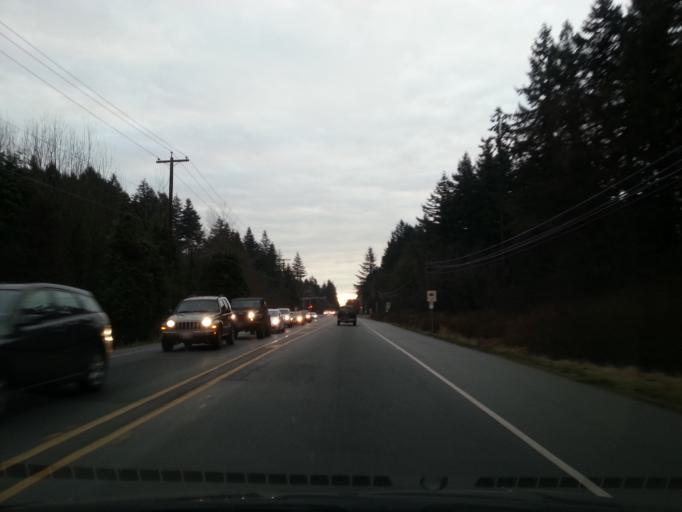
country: CA
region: British Columbia
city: Surrey
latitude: 49.1776
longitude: -122.8314
